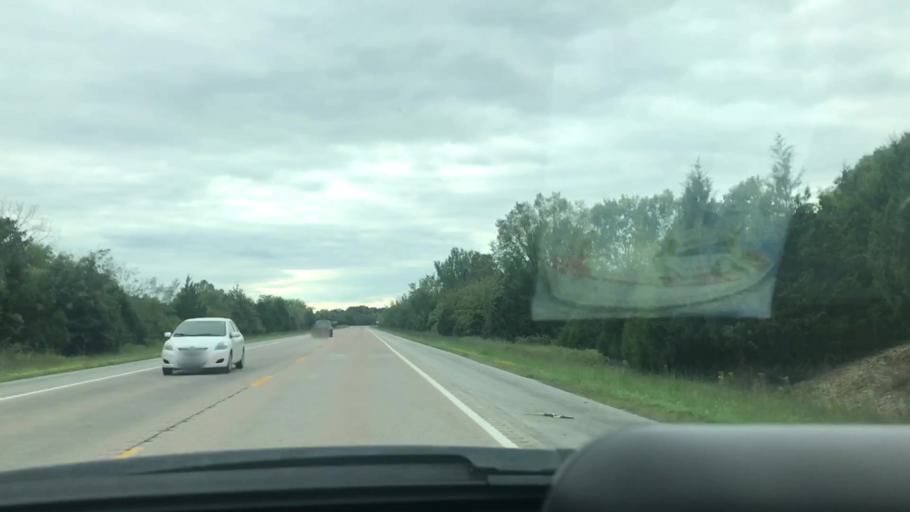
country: US
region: Missouri
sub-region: Benton County
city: Warsaw
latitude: 38.2101
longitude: -93.3362
